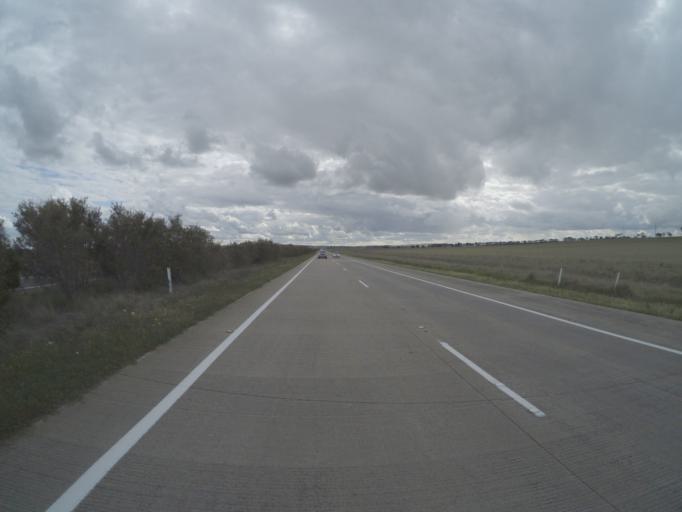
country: AU
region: New South Wales
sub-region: Goulburn Mulwaree
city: Goulburn
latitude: -34.8093
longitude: 149.5837
